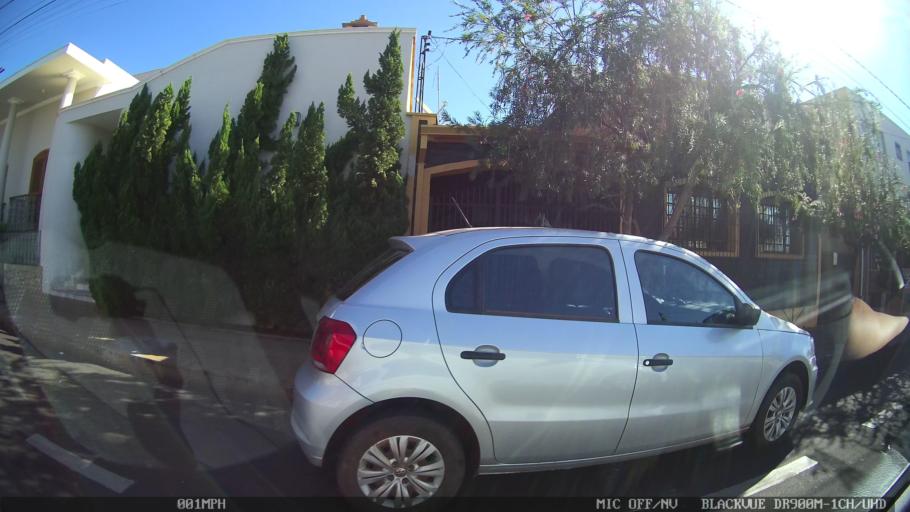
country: BR
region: Sao Paulo
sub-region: Olimpia
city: Olimpia
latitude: -20.7367
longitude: -48.9170
